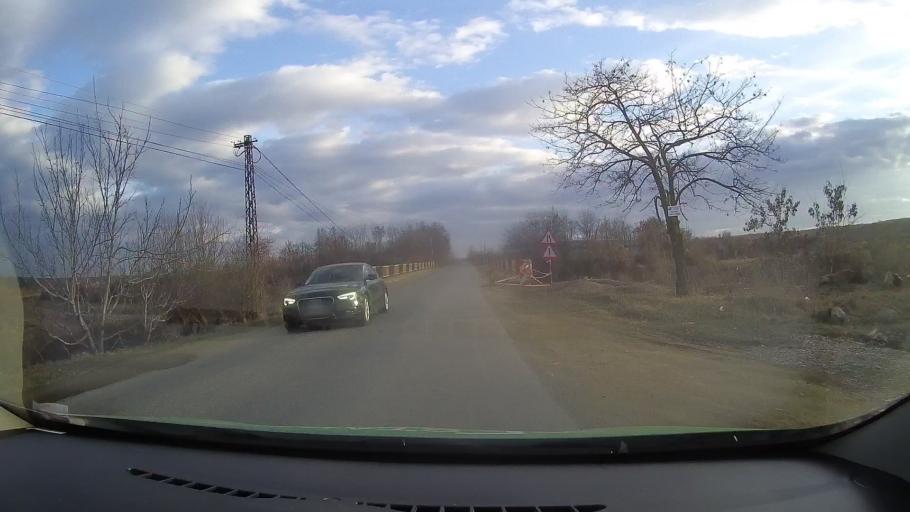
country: RO
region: Dambovita
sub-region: Comuna I. L. Caragiale
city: Ghirdoveni
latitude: 44.9593
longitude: 25.6573
